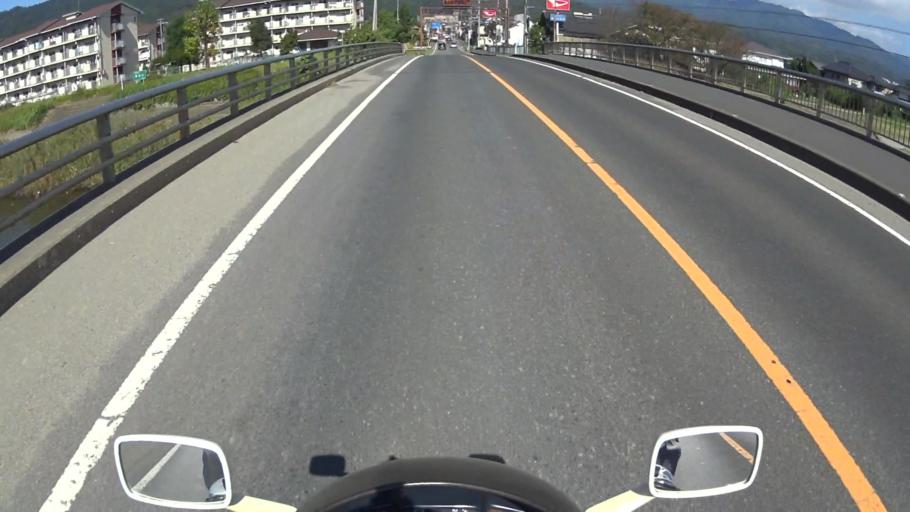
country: JP
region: Kyoto
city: Miyazu
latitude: 35.5591
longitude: 135.1534
